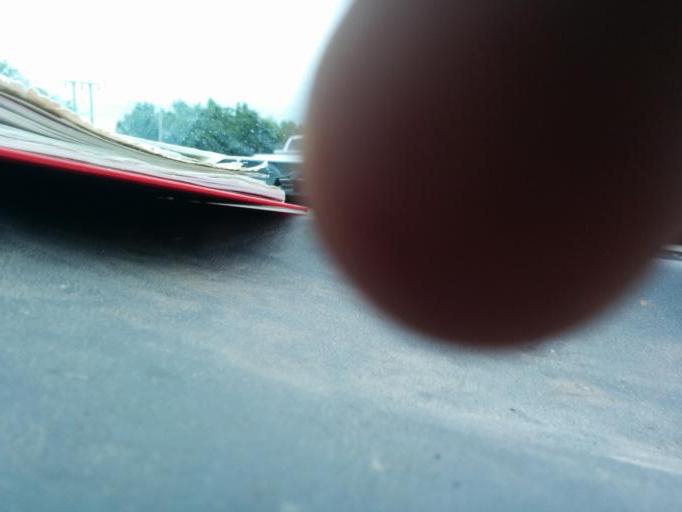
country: US
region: Oklahoma
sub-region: Tulsa County
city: Glenpool
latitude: 35.9720
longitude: -96.0119
